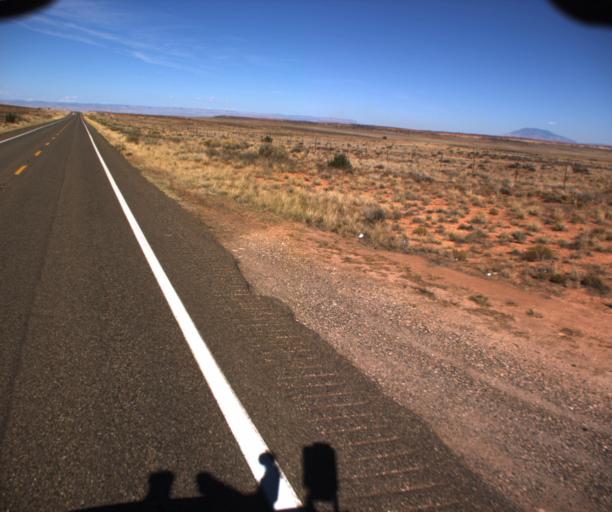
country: US
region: Arizona
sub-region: Coconino County
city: LeChee
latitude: 36.7453
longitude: -111.5773
